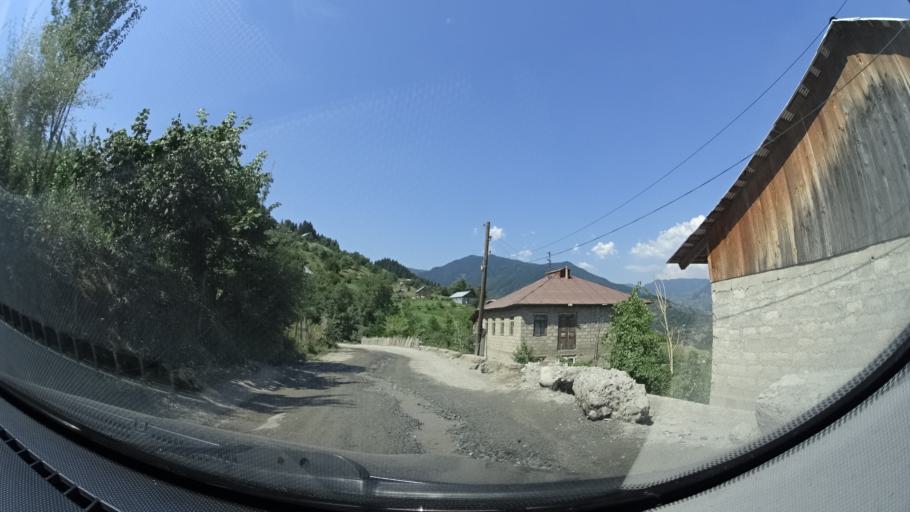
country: GE
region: Ajaria
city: Khulo
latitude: 41.6456
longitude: 42.3190
